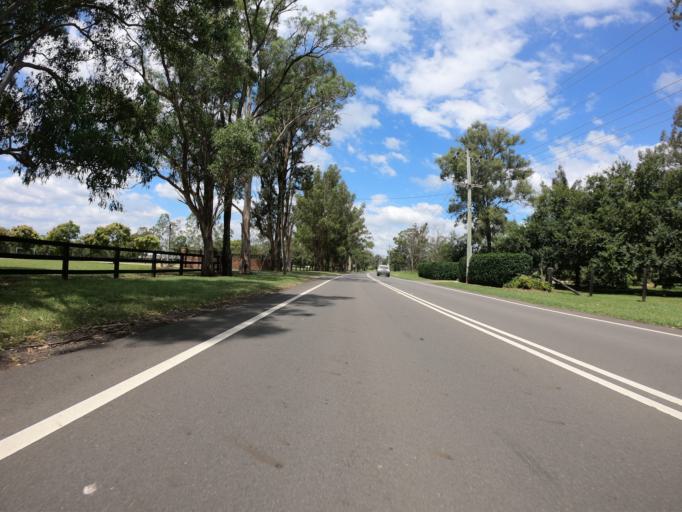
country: AU
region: New South Wales
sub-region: Penrith Municipality
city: Mulgoa
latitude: -33.8272
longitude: 150.6683
